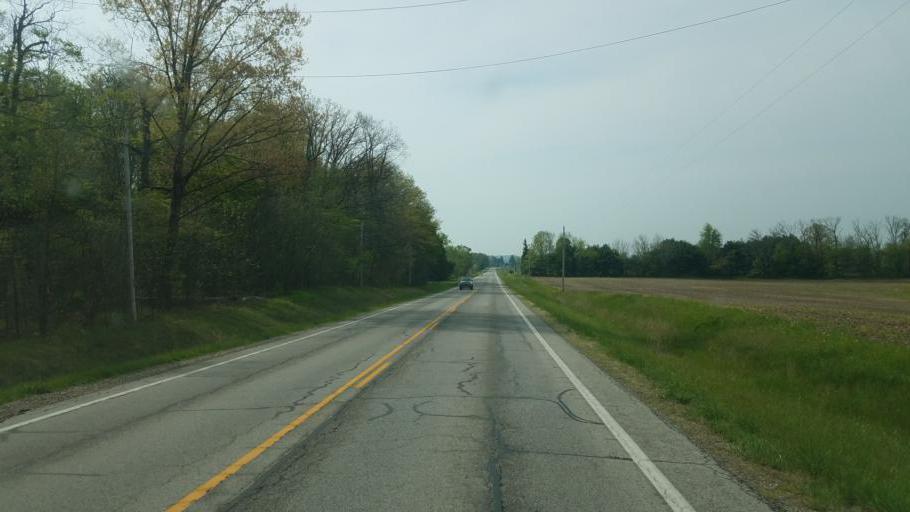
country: US
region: Ohio
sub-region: Licking County
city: Utica
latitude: 40.3111
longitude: -82.4578
